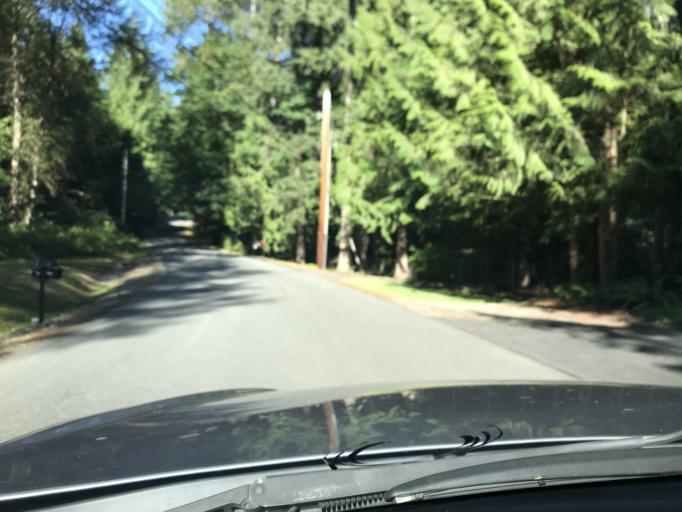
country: US
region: Washington
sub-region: King County
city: Maple Heights-Lake Desire
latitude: 47.4409
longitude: -122.0899
